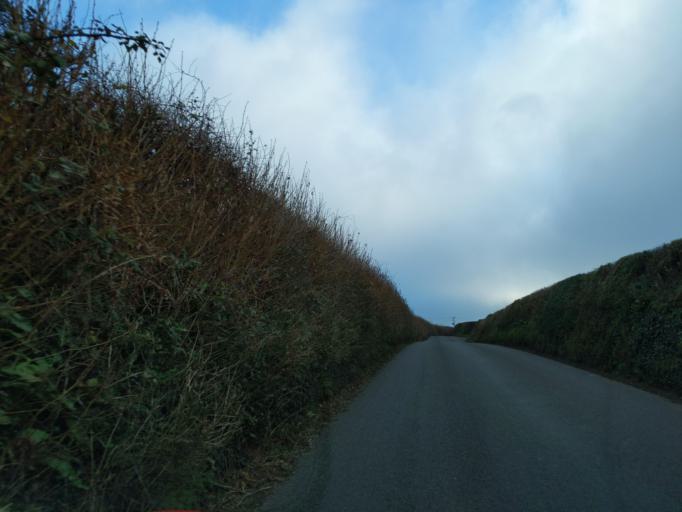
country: GB
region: England
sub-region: Cornwall
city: Pillaton
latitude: 50.3711
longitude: -4.3026
